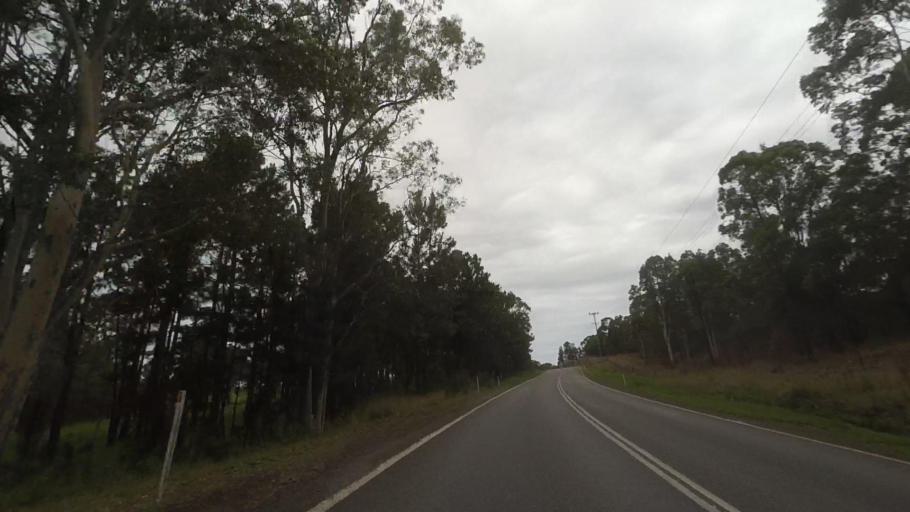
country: AU
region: New South Wales
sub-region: Great Lakes
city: Hawks Nest
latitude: -32.6171
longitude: 152.1110
